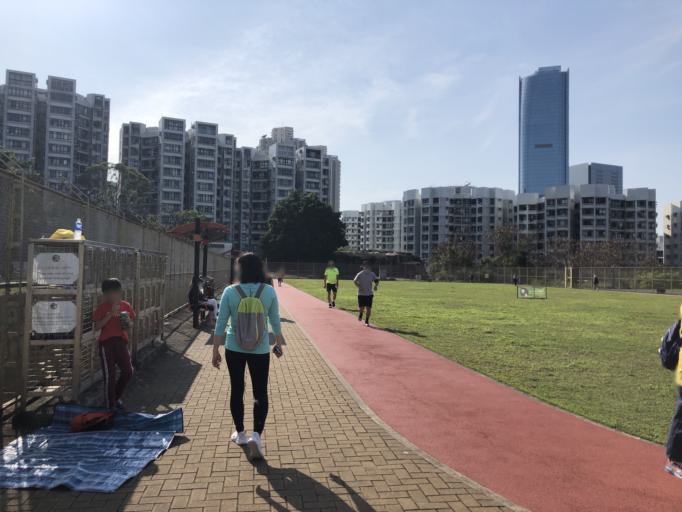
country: HK
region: Wanchai
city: Wan Chai
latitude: 22.2818
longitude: 114.2179
